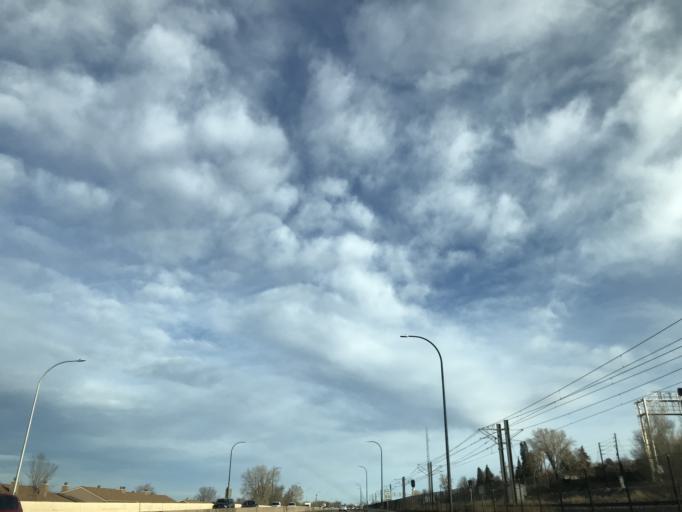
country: US
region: Colorado
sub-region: Arapahoe County
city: Columbine Valley
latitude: 39.5874
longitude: -105.0228
